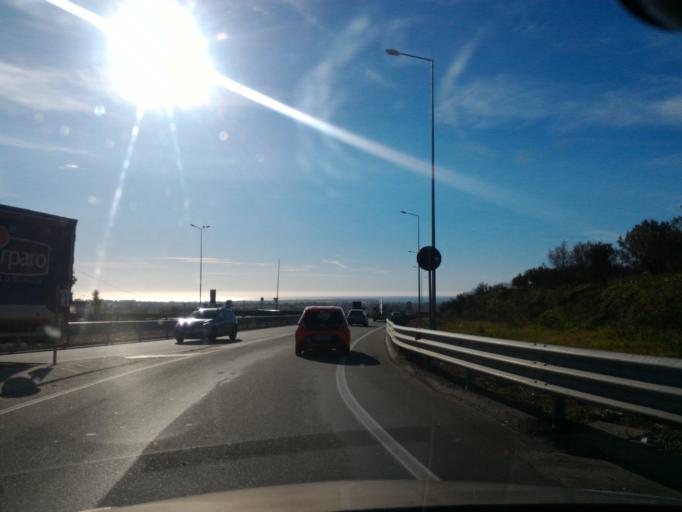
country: IT
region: Calabria
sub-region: Provincia di Crotone
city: Isola di Capo Rizzuto
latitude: 38.9503
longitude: 17.0826
